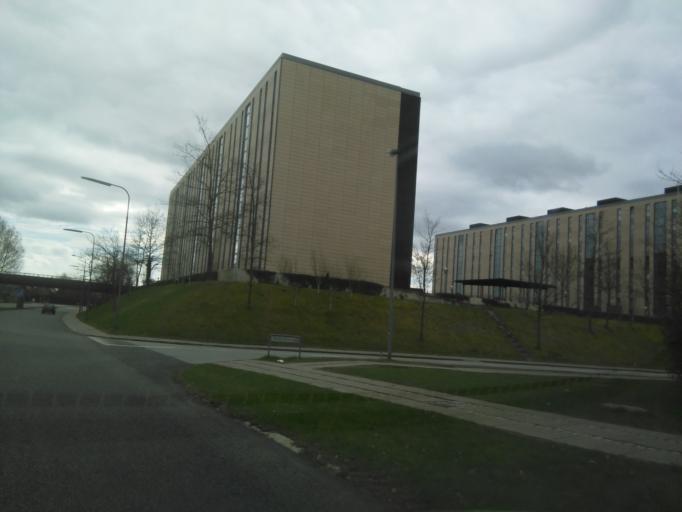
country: DK
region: Central Jutland
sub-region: Arhus Kommune
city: Stavtrup
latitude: 56.1678
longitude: 10.1564
